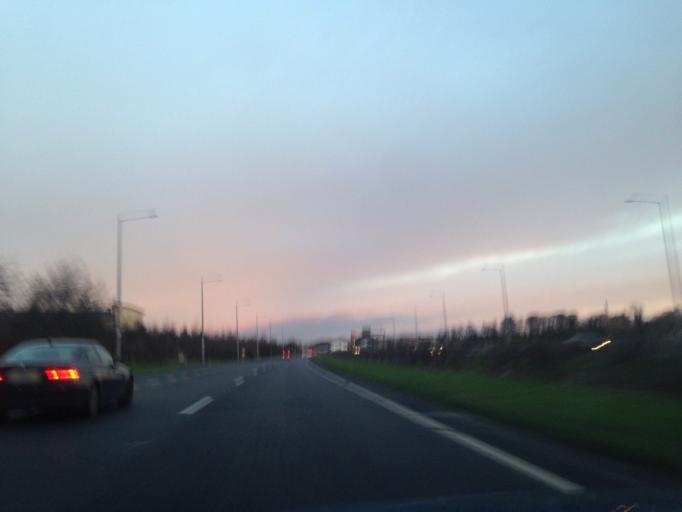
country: IE
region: Leinster
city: Foxrock
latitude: 53.2555
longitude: -6.1820
